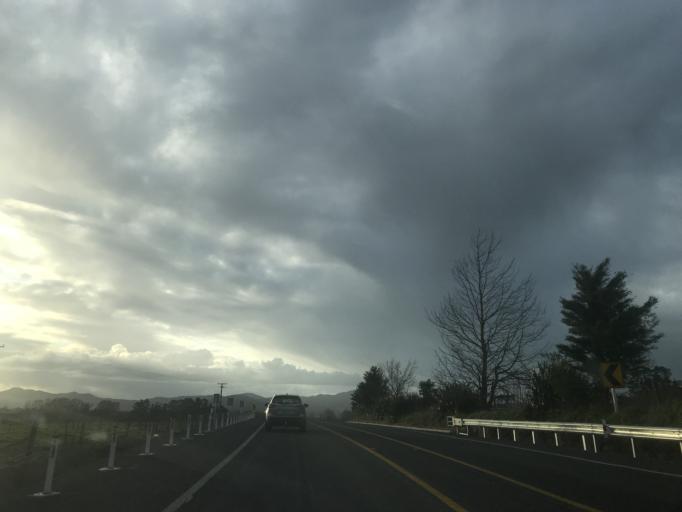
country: NZ
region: Bay of Plenty
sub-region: Western Bay of Plenty District
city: Waihi Beach
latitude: -37.4454
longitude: 175.8777
